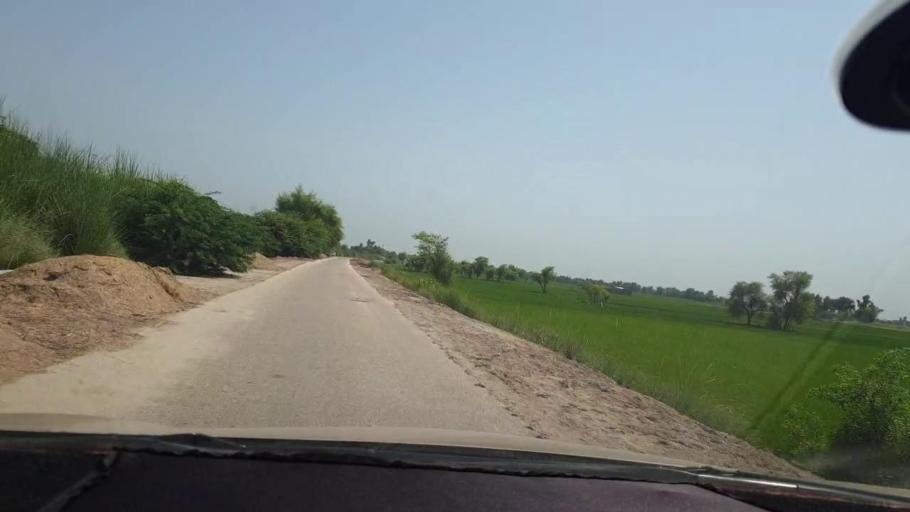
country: PK
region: Sindh
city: Kambar
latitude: 27.5190
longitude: 68.0094
